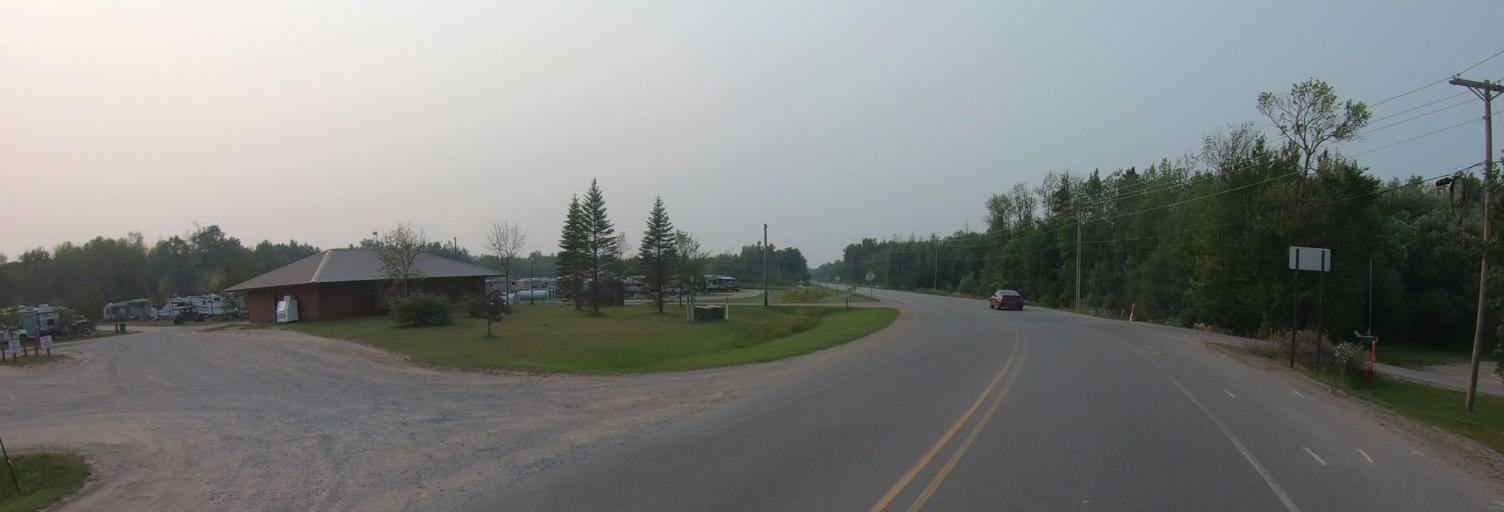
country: US
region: Michigan
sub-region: Chippewa County
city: Sault Ste. Marie
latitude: 46.4237
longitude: -84.6038
